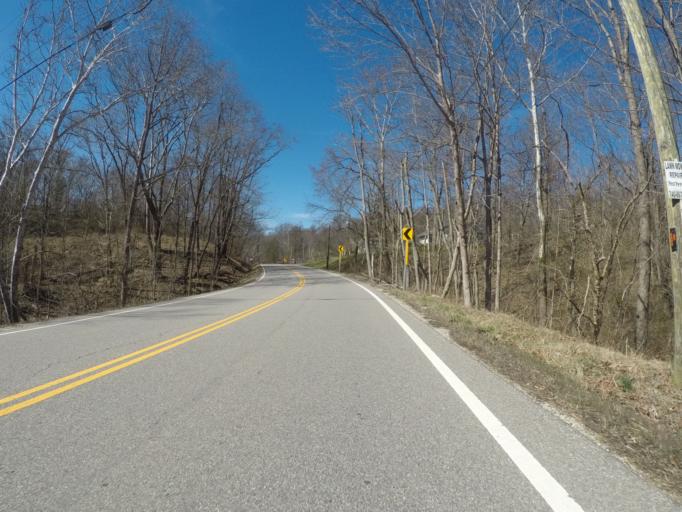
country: US
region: Ohio
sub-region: Lawrence County
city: South Point
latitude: 38.4877
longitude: -82.5520
